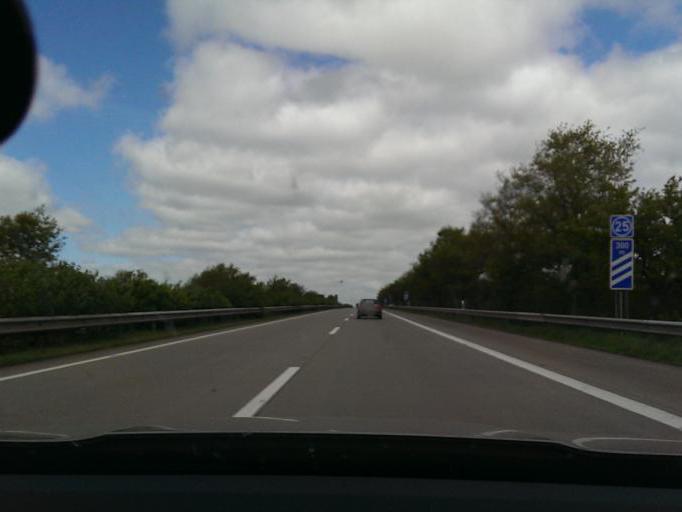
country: DE
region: Lower Saxony
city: Verden
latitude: 52.9534
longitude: 9.2514
